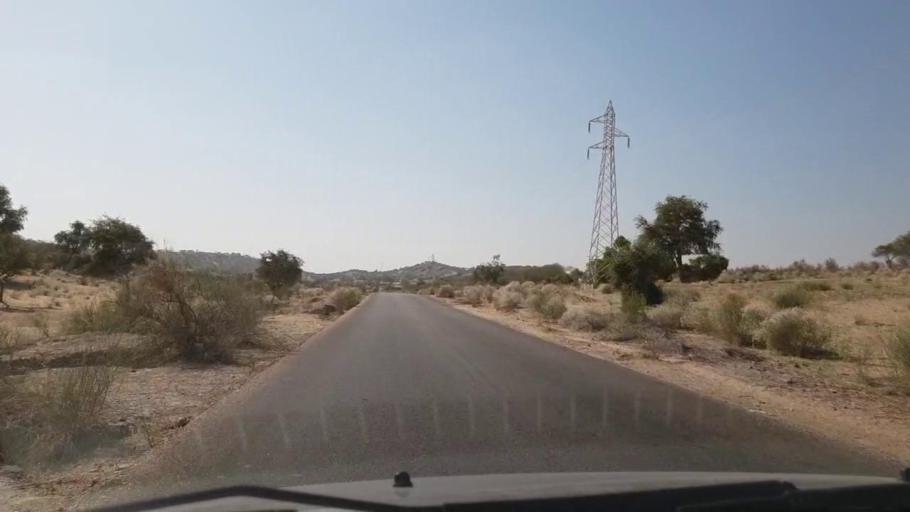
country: PK
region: Sindh
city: Mithi
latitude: 24.6844
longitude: 69.7832
